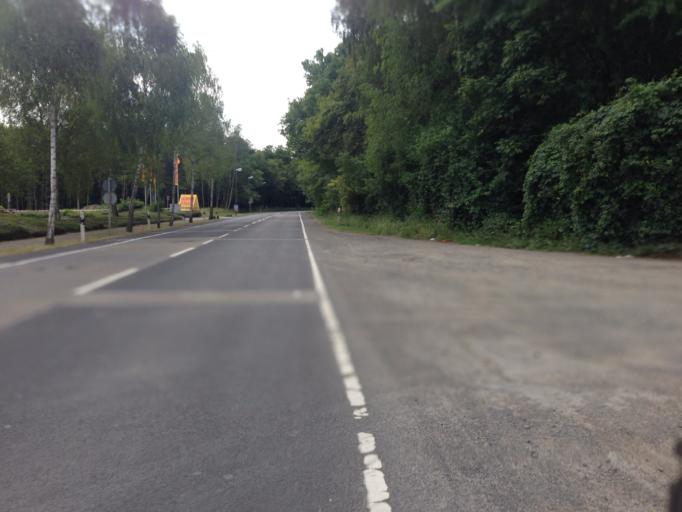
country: DE
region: Hesse
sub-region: Regierungsbezirk Darmstadt
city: Erlensee
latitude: 50.1467
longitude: 8.9508
